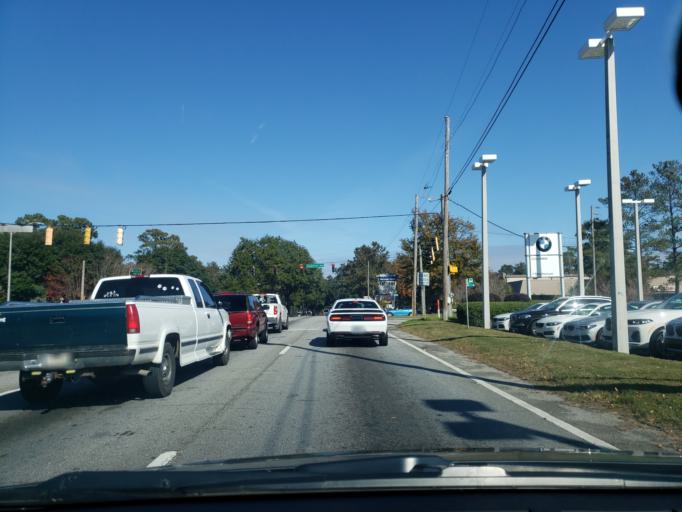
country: US
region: Georgia
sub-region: Chatham County
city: Isle of Hope
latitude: 32.0139
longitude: -81.1158
